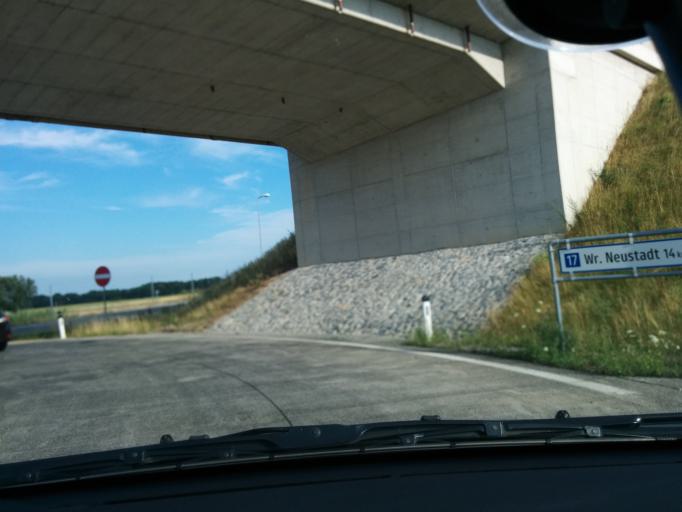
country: AT
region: Lower Austria
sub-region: Politischer Bezirk Baden
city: Schonau an der Triesting
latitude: 47.9167
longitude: 16.2581
